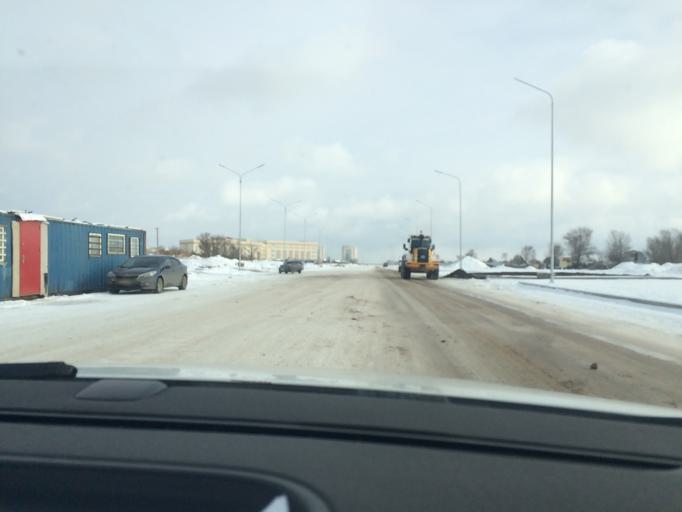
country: KZ
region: Astana Qalasy
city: Astana
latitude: 51.1216
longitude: 71.4888
